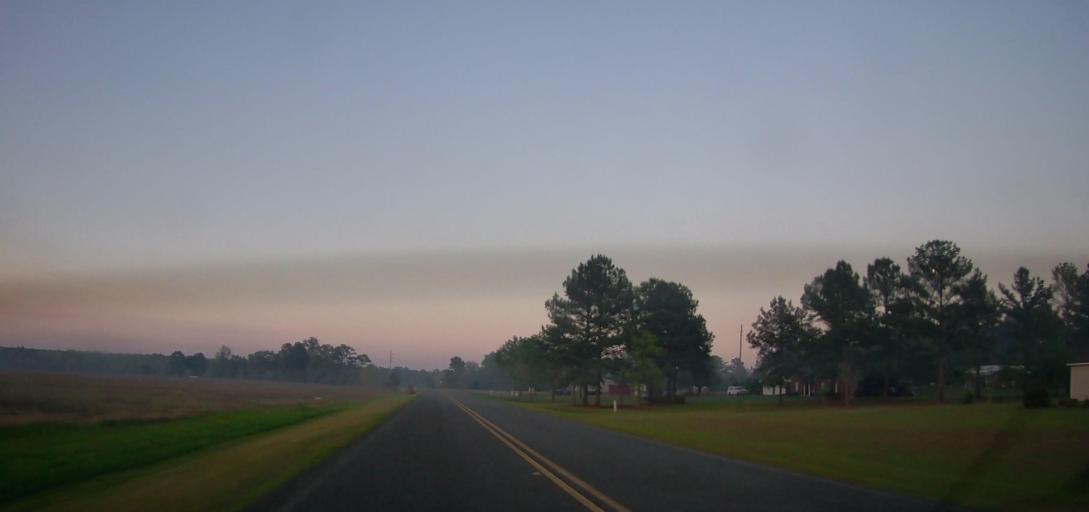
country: US
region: Georgia
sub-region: Marion County
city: Buena Vista
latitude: 32.2633
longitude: -84.5565
